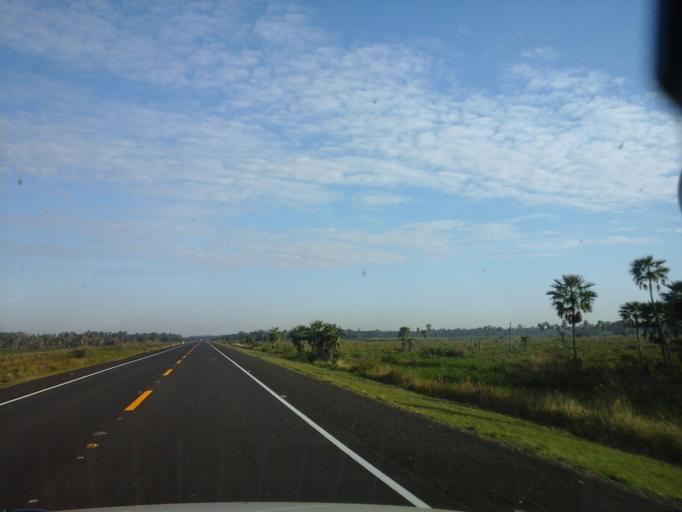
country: PY
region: Neembucu
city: Cerrito
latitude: -26.8773
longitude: -57.7465
